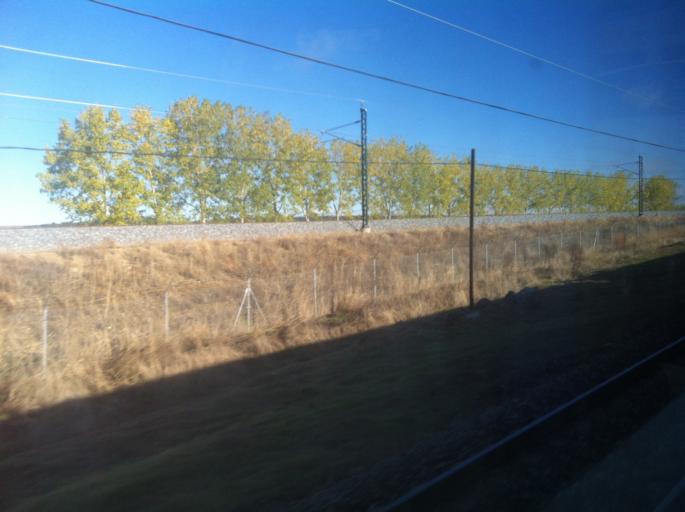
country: ES
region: Castille and Leon
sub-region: Provincia de Palencia
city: Villodrigo
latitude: 42.1552
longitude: -4.0921
